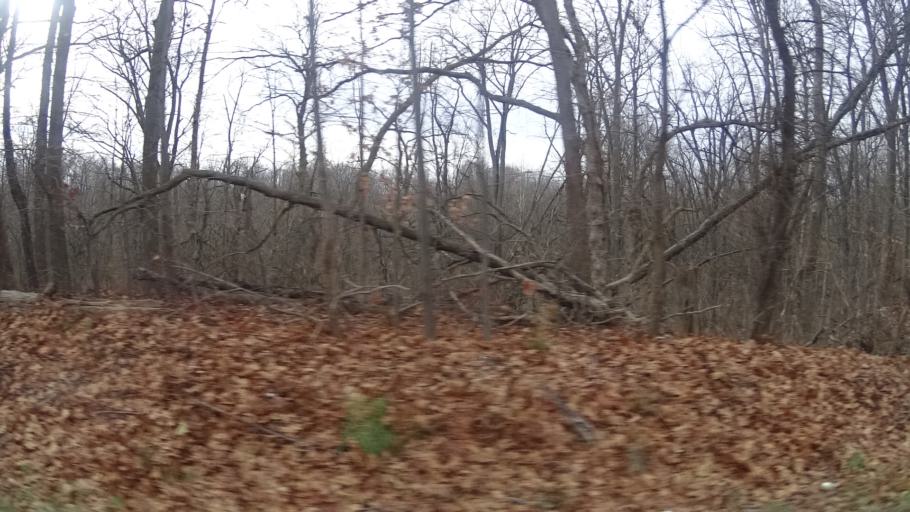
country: US
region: Ohio
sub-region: Cuyahoga County
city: Olmsted Falls
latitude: 41.3052
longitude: -81.9131
